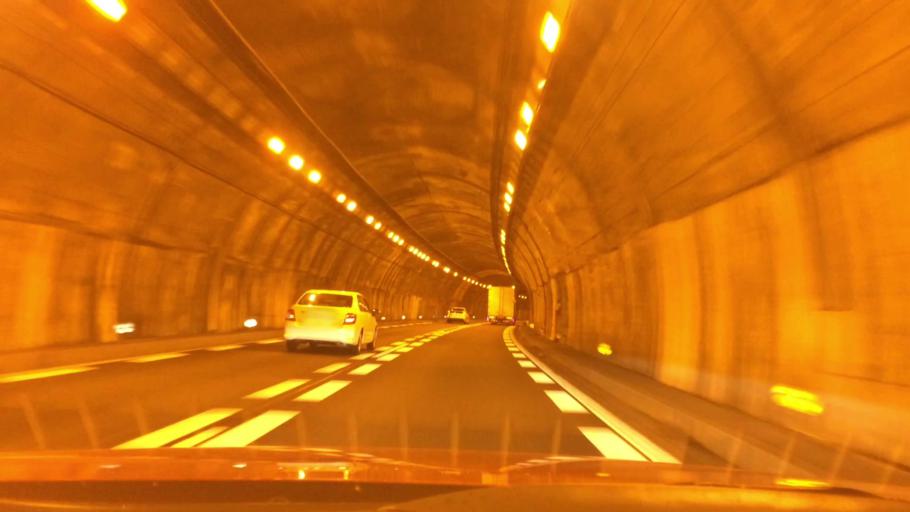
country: JP
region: Gifu
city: Tarui
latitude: 35.3474
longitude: 136.4436
